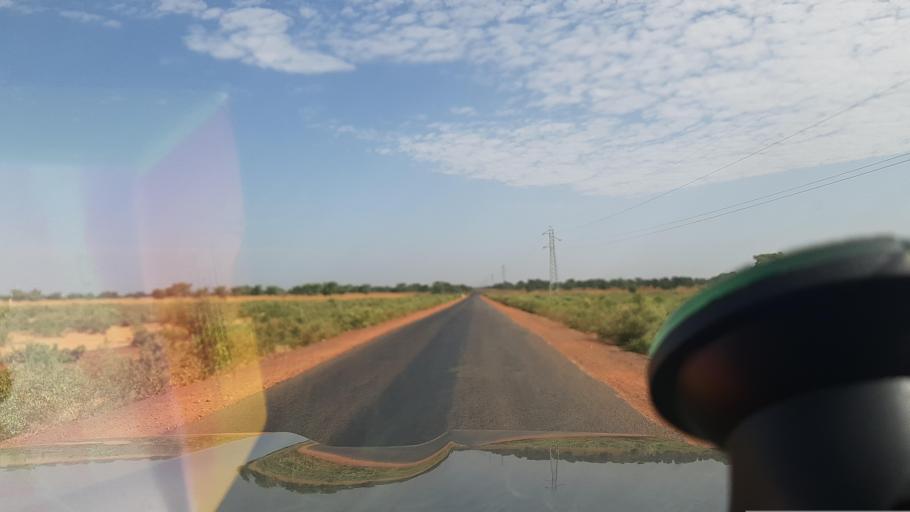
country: ML
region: Segou
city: Segou
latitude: 13.5507
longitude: -6.1168
